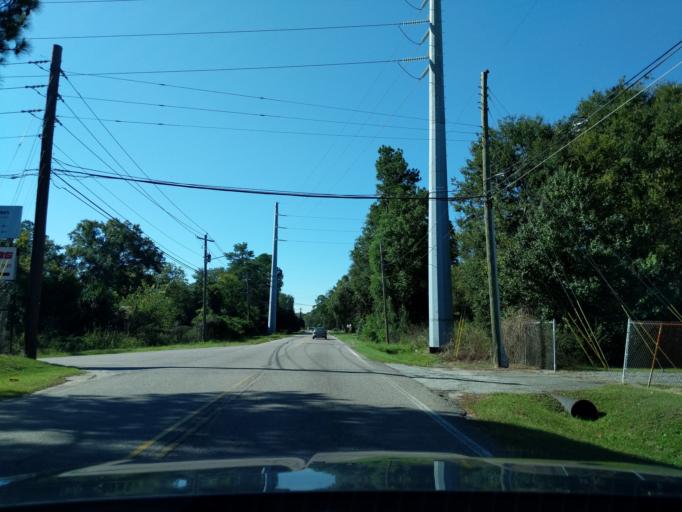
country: US
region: Georgia
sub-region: Richmond County
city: Augusta
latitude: 33.4346
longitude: -82.0033
